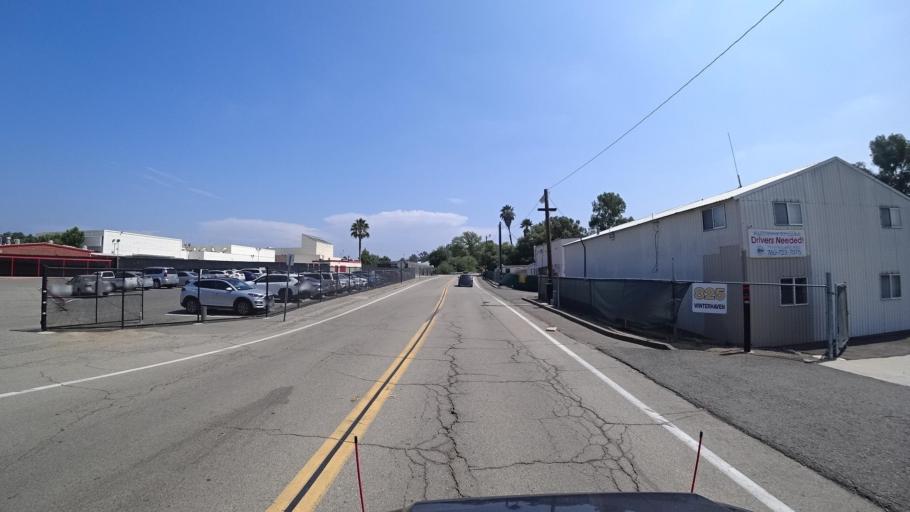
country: US
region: California
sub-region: San Diego County
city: Fallbrook
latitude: 33.3469
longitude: -117.2415
